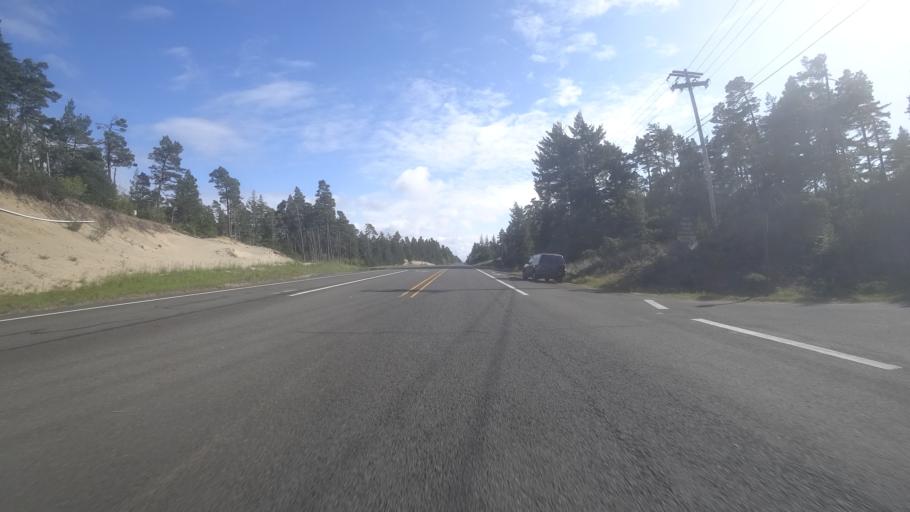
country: US
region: Oregon
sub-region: Lane County
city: Florence
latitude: 44.0451
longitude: -124.0988
